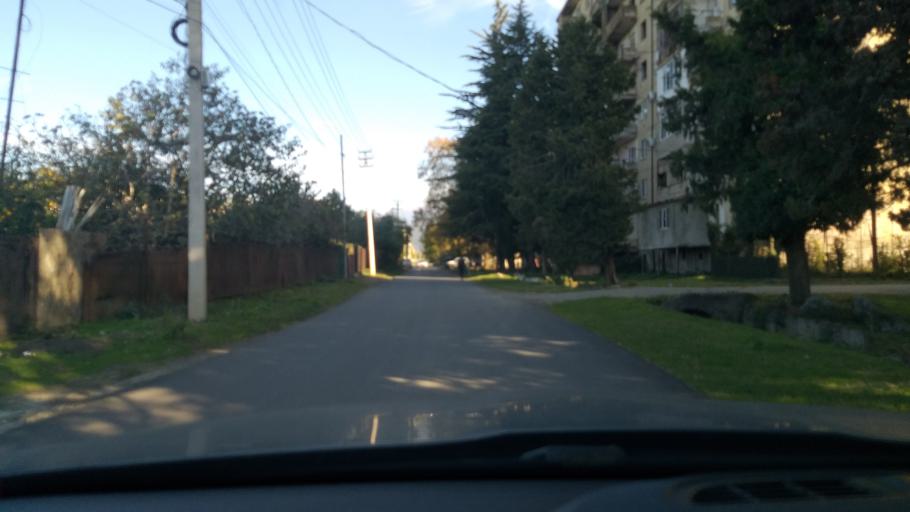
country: GE
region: Abkhazia
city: Sokhumi
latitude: 43.0153
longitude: 40.9635
